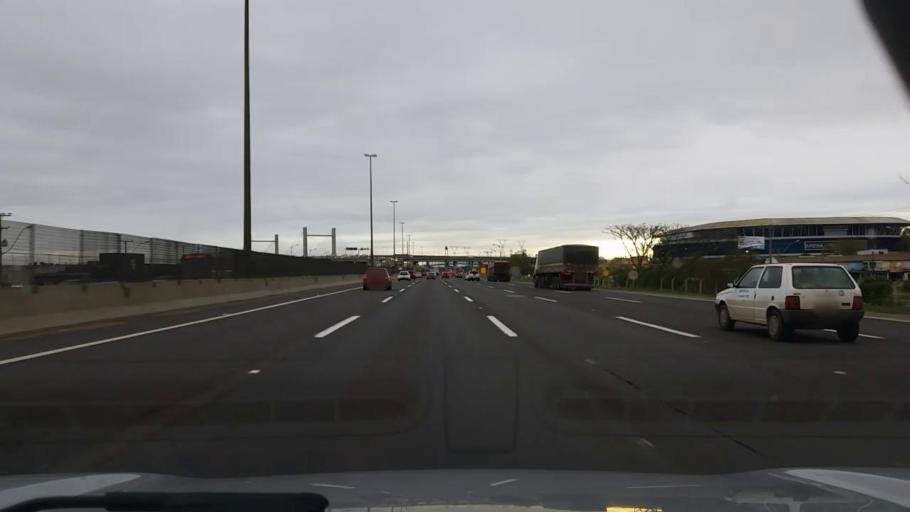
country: BR
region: Rio Grande do Sul
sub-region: Porto Alegre
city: Porto Alegre
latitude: -29.9801
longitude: -51.2008
